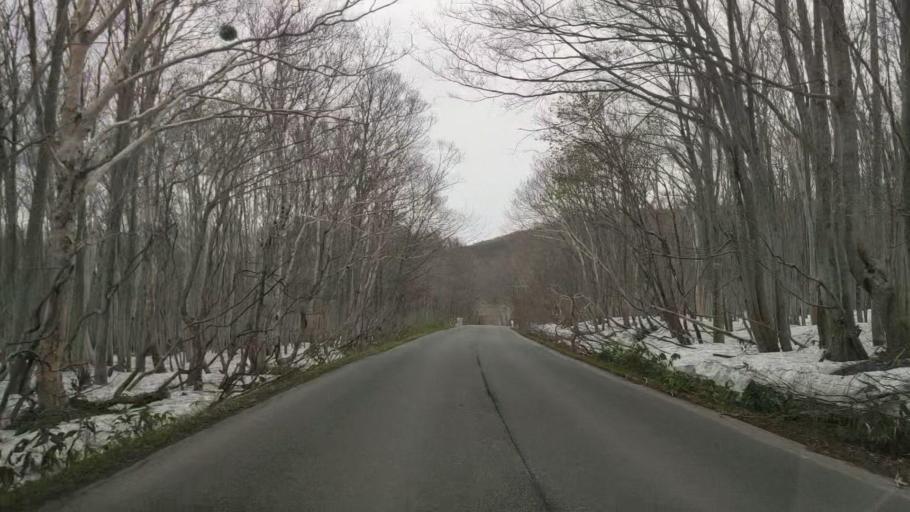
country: JP
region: Aomori
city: Aomori Shi
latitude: 40.6953
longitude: 140.9072
